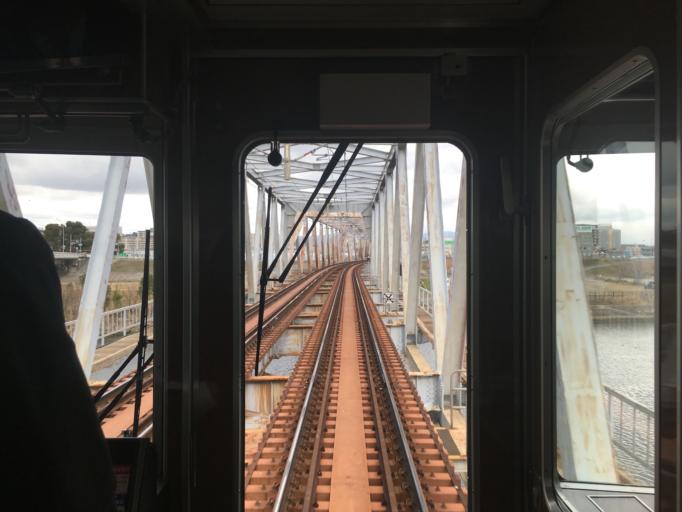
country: JP
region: Osaka
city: Osaka-shi
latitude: 34.7228
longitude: 135.5106
